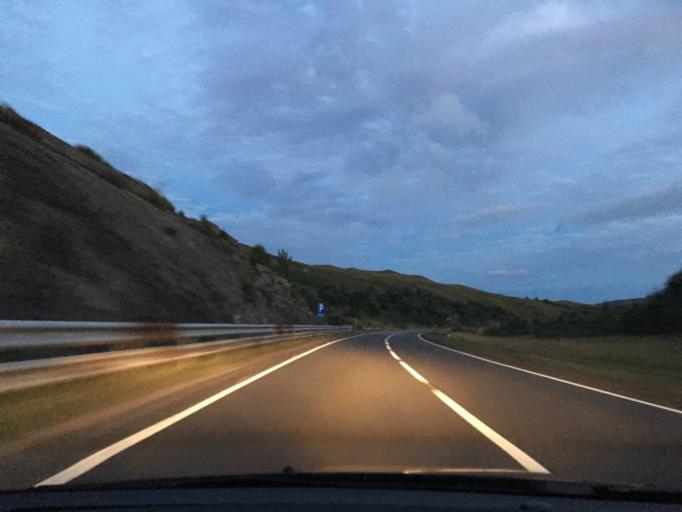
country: GB
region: Scotland
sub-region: Perth and Kinross
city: Aberfeldy
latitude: 56.7958
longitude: -4.0178
